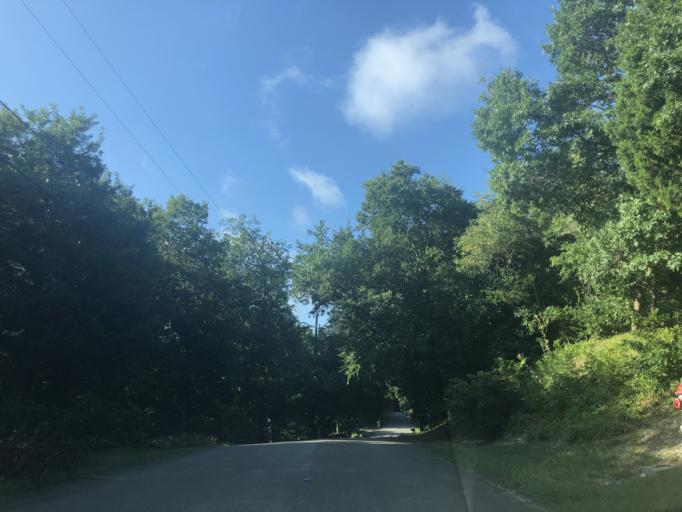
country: US
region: Texas
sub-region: Dallas County
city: Duncanville
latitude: 32.6726
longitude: -96.9237
